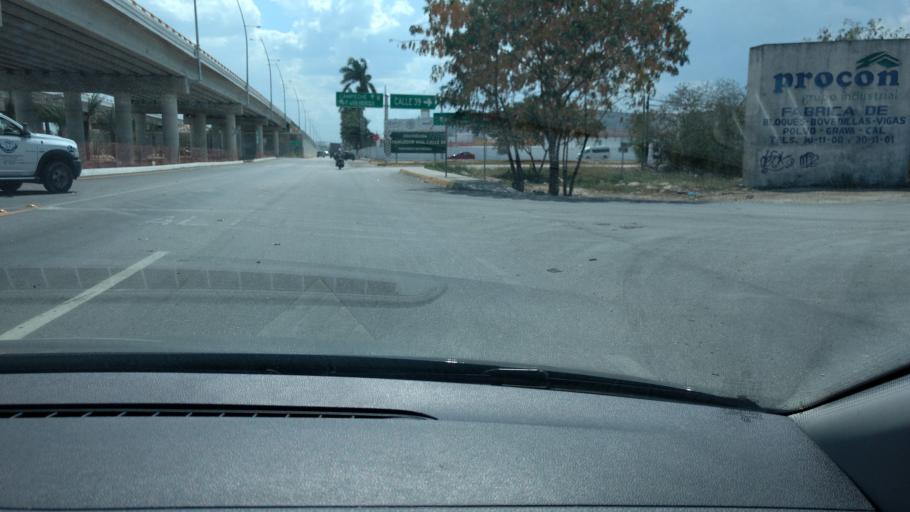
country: MX
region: Yucatan
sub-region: Kanasin
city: Kanasin
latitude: 20.9826
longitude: -89.5640
